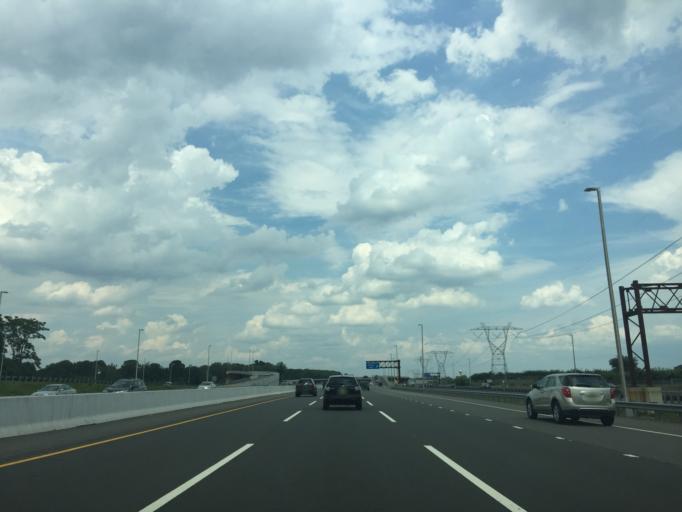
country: US
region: New Jersey
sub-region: Mercer County
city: Yardville
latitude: 40.1666
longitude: -74.6468
